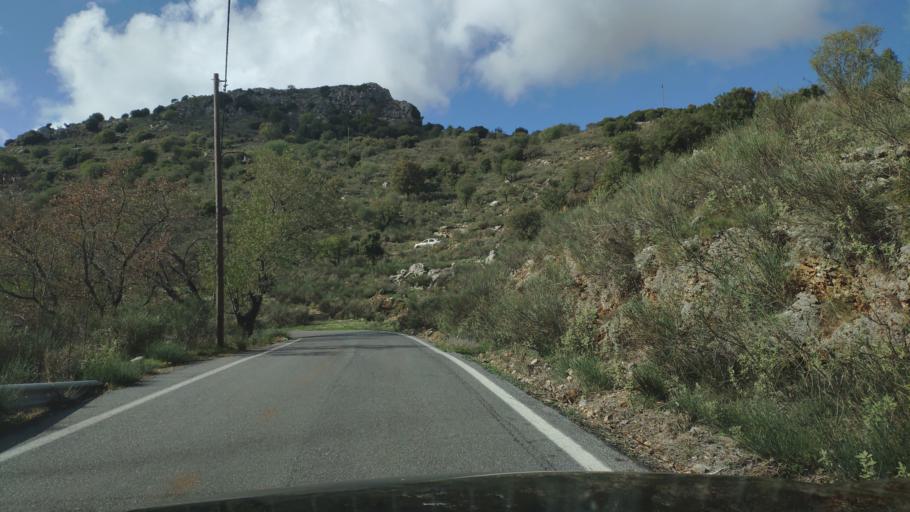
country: GR
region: Peloponnese
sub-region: Nomos Arkadias
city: Dimitsana
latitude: 37.5928
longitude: 22.0300
